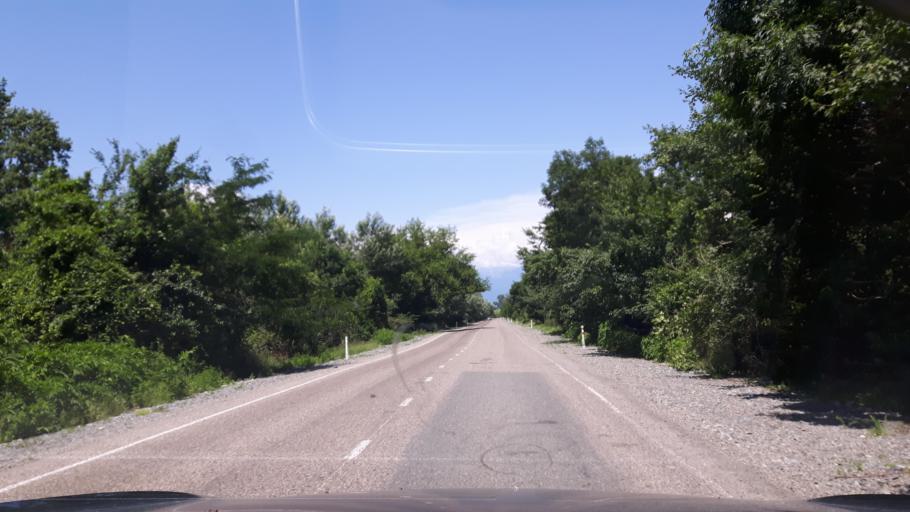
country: GE
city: Tsnori
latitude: 41.6803
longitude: 46.0837
